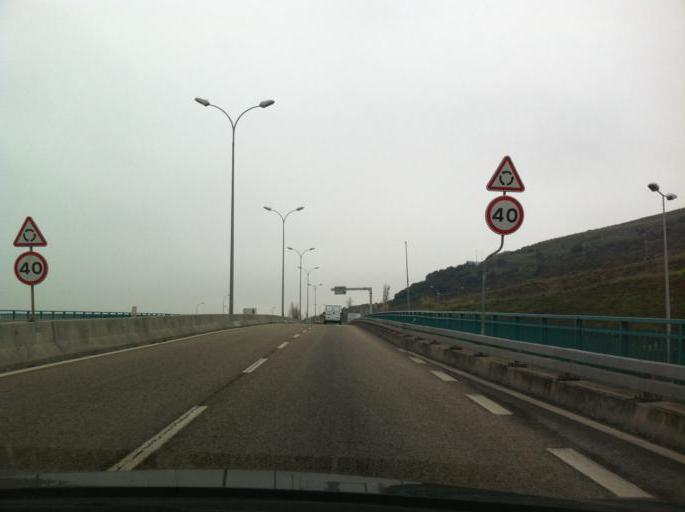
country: PT
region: Lisbon
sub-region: Odivelas
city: Famoes
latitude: 38.7756
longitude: -9.2233
